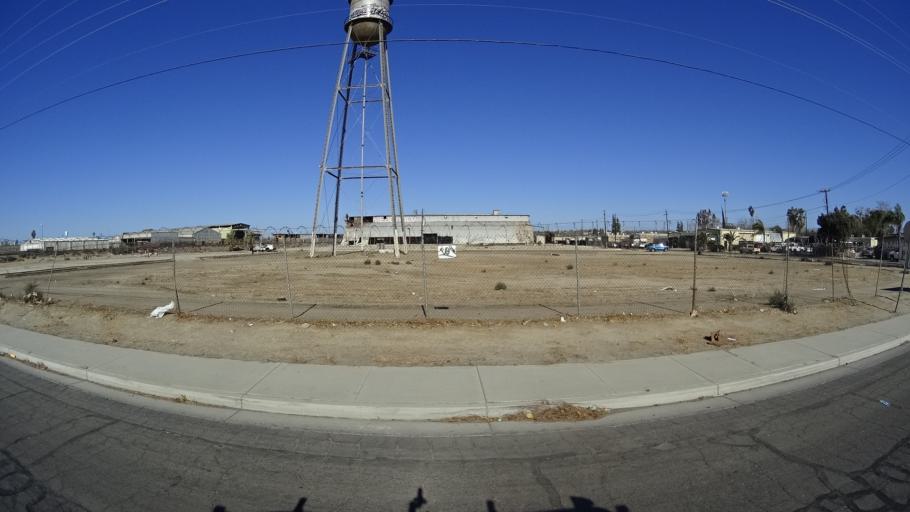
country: US
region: California
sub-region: Kern County
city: Bakersfield
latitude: 35.3686
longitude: -118.9771
